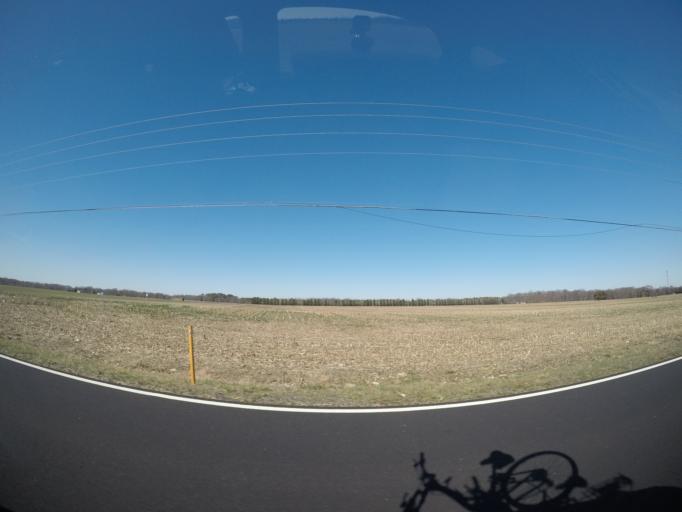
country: US
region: Delaware
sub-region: New Castle County
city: Townsend
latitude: 39.3568
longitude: -75.8336
